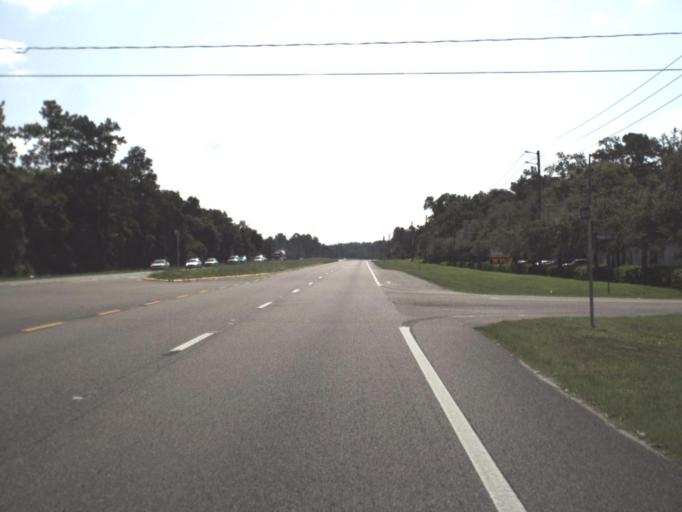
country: US
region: Florida
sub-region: Hernando County
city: South Brooksville
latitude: 28.5381
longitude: -82.3926
